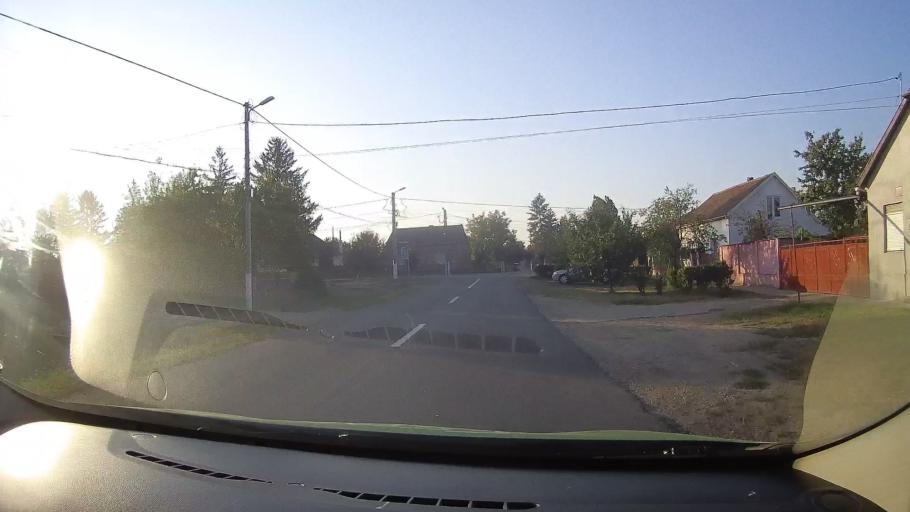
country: RO
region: Arad
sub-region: Comuna Curtici
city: Curtici
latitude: 46.3347
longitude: 21.3055
